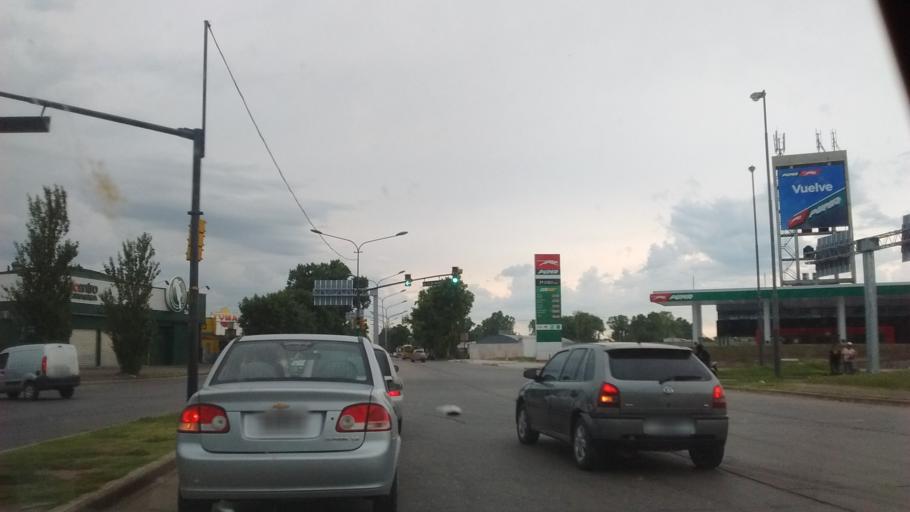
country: AR
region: Santa Fe
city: Perez
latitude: -32.9705
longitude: -60.7164
